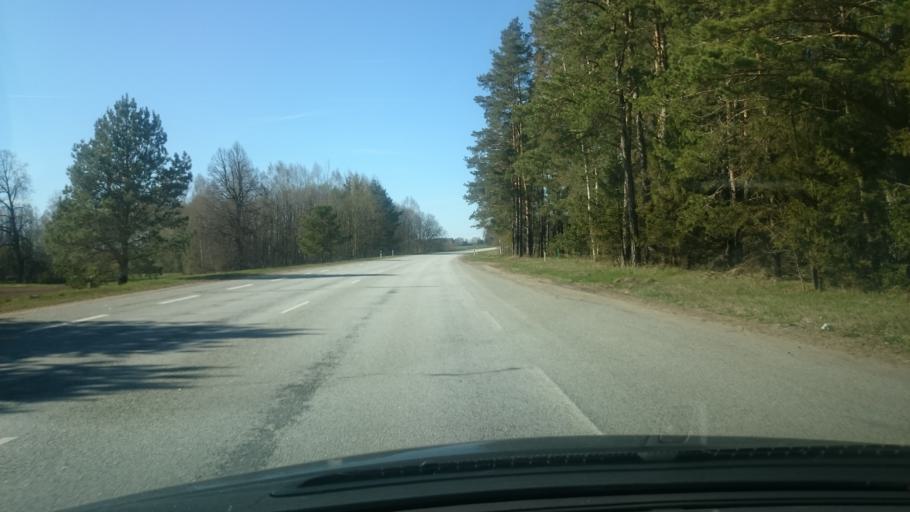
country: EE
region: Tartu
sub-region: UElenurme vald
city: Ulenurme
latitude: 58.3150
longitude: 26.9888
